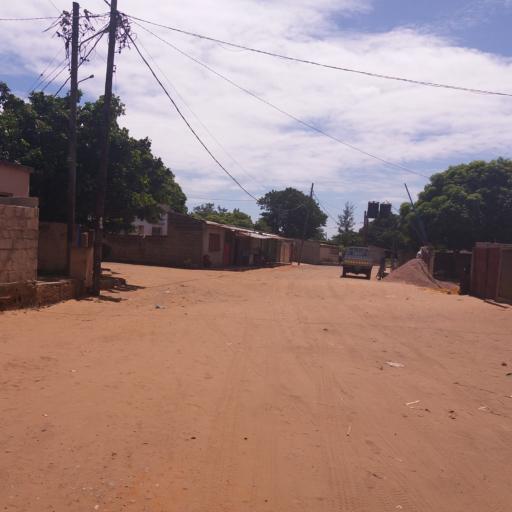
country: MZ
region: Maputo City
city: Maputo
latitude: -25.9067
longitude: 32.5900
